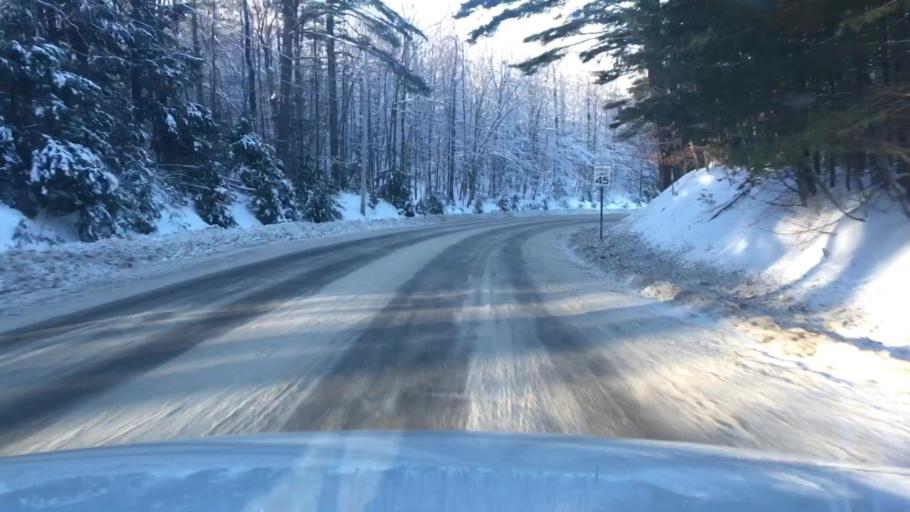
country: US
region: Maine
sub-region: Kennebec County
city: Readfield
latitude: 44.4301
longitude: -69.9617
